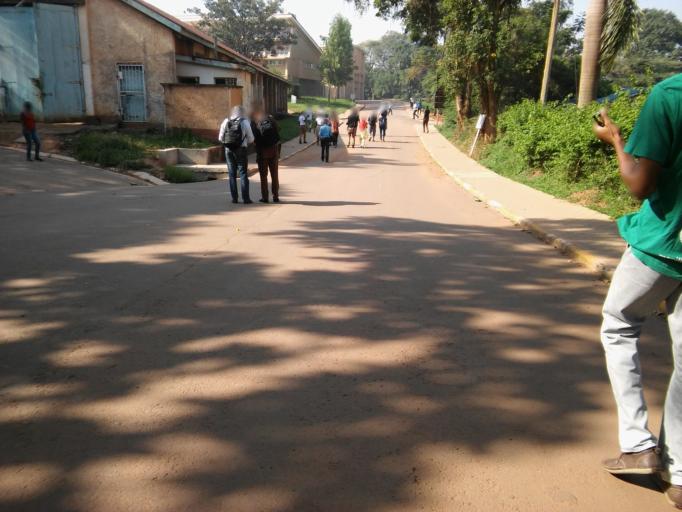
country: UG
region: Central Region
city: Kampala Central Division
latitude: 0.3362
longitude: 32.5651
